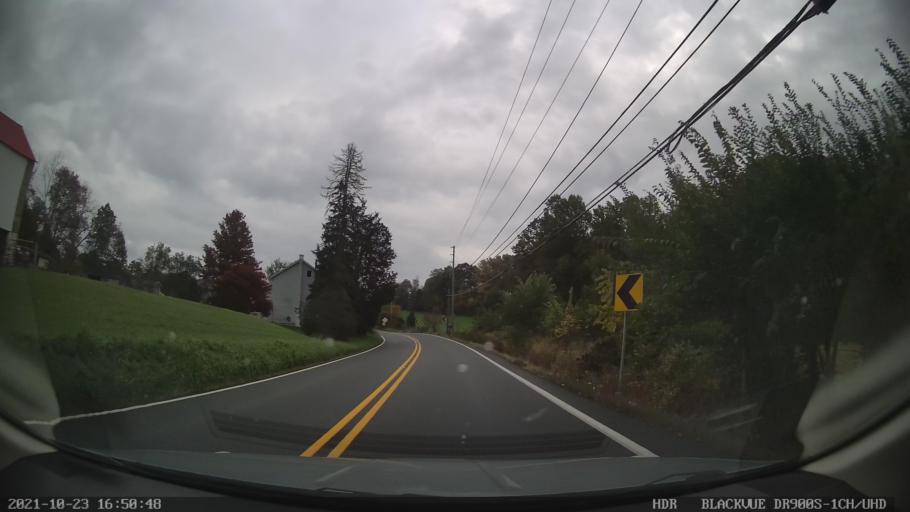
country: US
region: Pennsylvania
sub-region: Berks County
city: Red Lion
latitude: 40.4759
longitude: -75.6114
